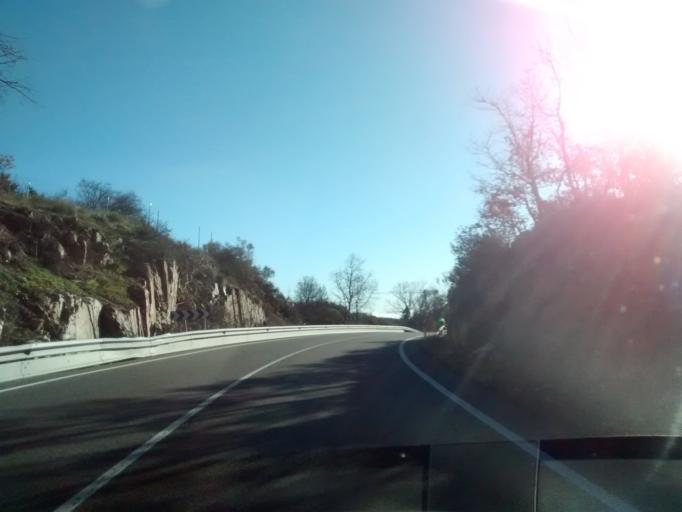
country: ES
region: Madrid
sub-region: Provincia de Madrid
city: Navacerrada
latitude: 40.7354
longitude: -4.0095
